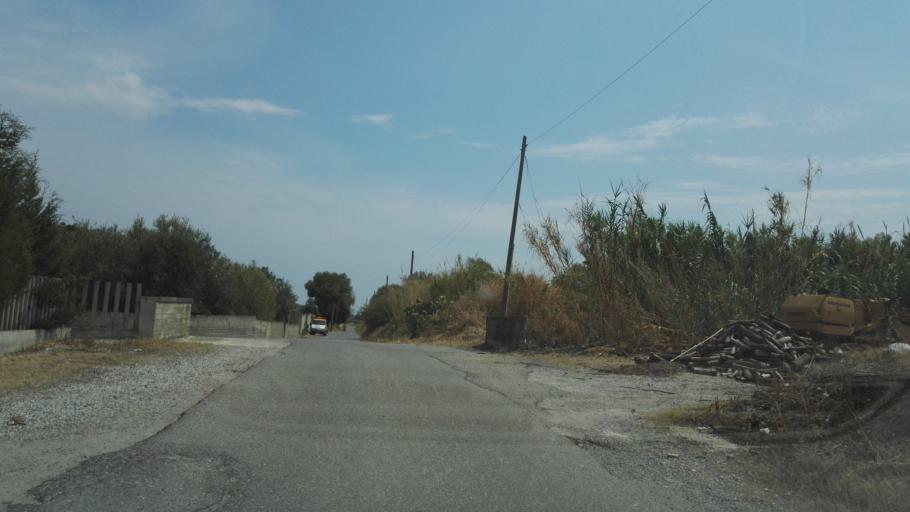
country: IT
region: Calabria
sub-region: Provincia di Reggio Calabria
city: Monasterace Marina
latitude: 38.4310
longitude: 16.5580
